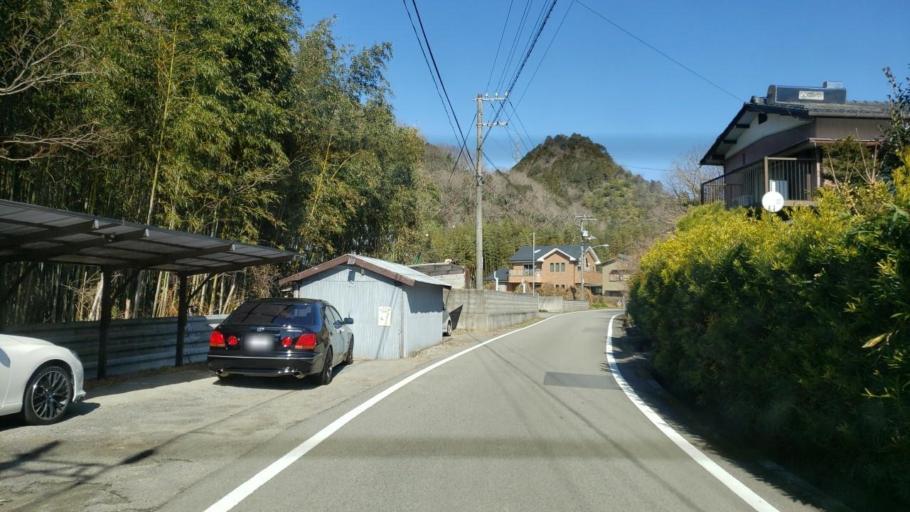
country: JP
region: Tokushima
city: Narutocho-mitsuishi
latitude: 34.1748
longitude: 134.5427
